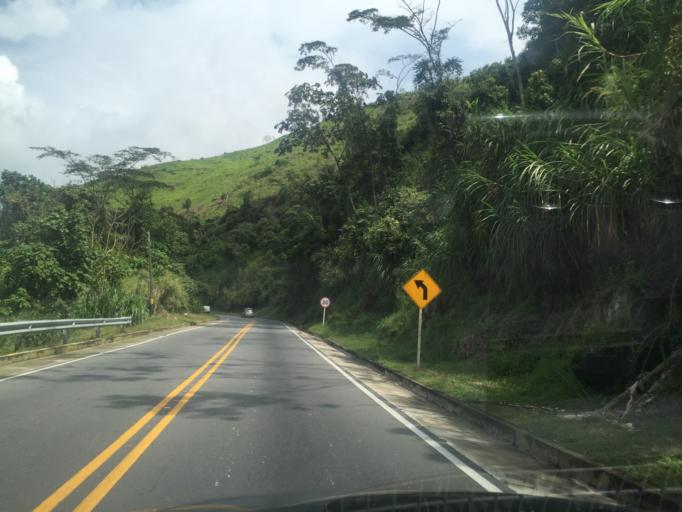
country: CO
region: Caldas
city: Chinchina
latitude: 5.0093
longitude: -75.5627
